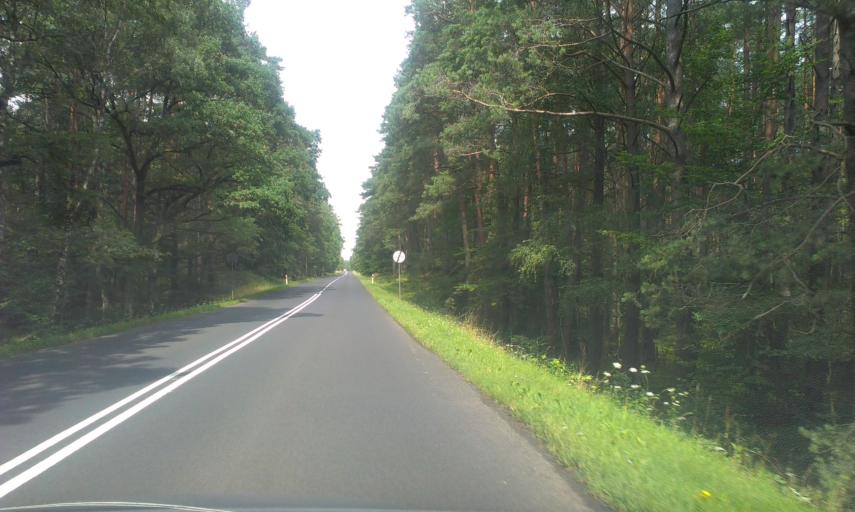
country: PL
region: West Pomeranian Voivodeship
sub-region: Powiat bialogardzki
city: Bialogard
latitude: 53.9362
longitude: 16.0613
